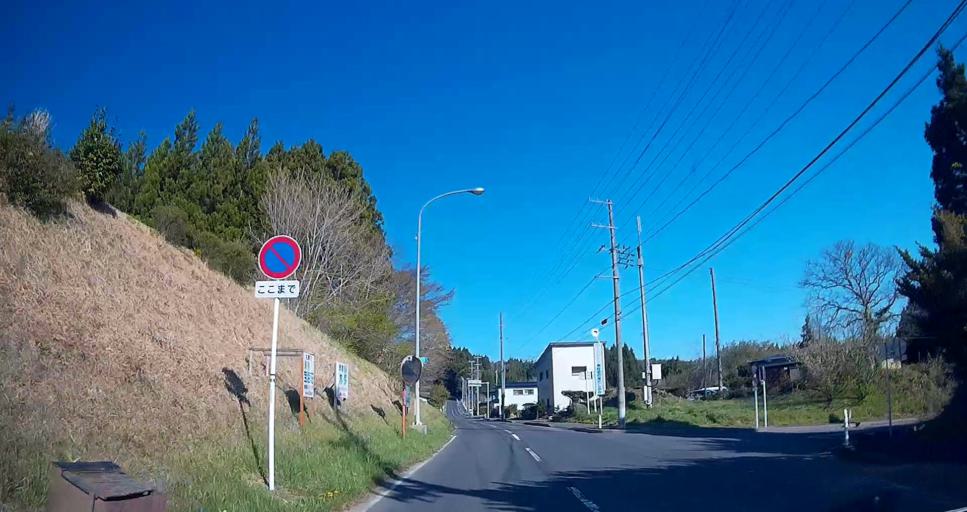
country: JP
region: Aomori
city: Hachinohe
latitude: 40.5177
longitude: 141.5854
